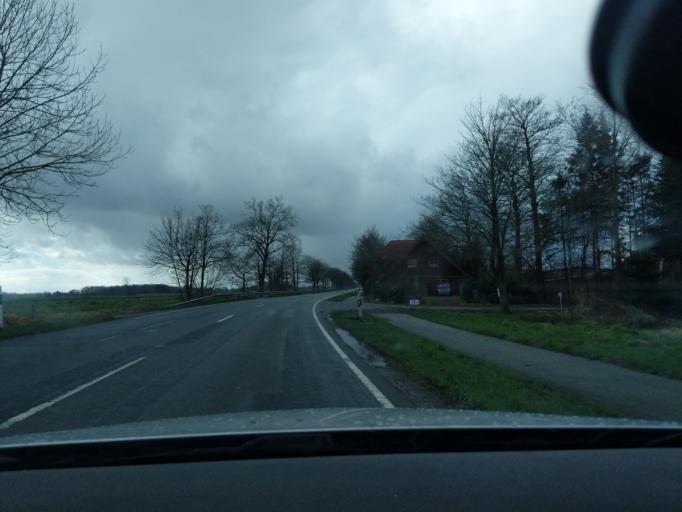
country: DE
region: Lower Saxony
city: Osten
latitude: 53.7210
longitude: 9.2390
